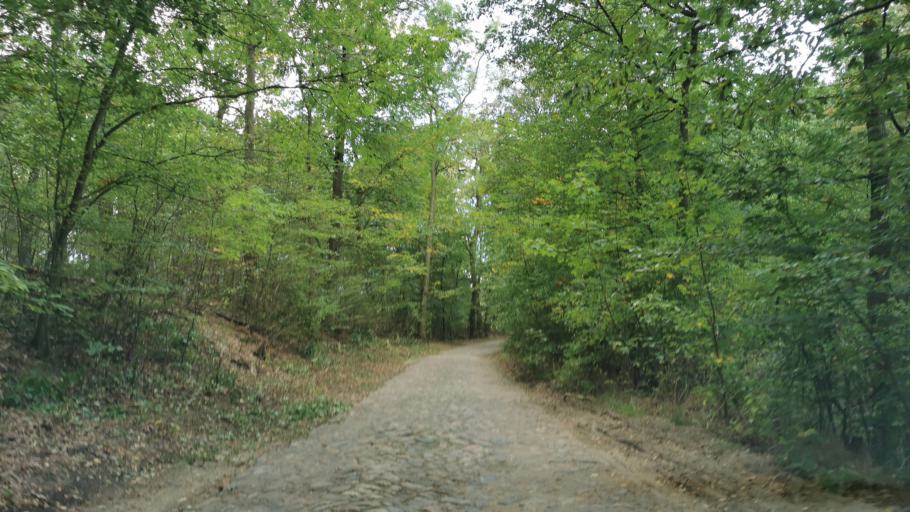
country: DE
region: Brandenburg
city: Michendorf
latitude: 52.3055
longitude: 12.9705
